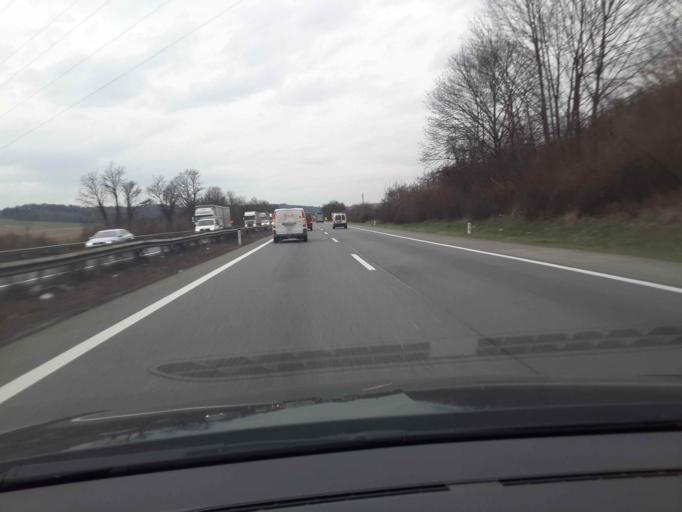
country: AT
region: Lower Austria
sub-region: Politischer Bezirk Melk
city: Leiben
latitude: 48.2061
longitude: 15.2698
